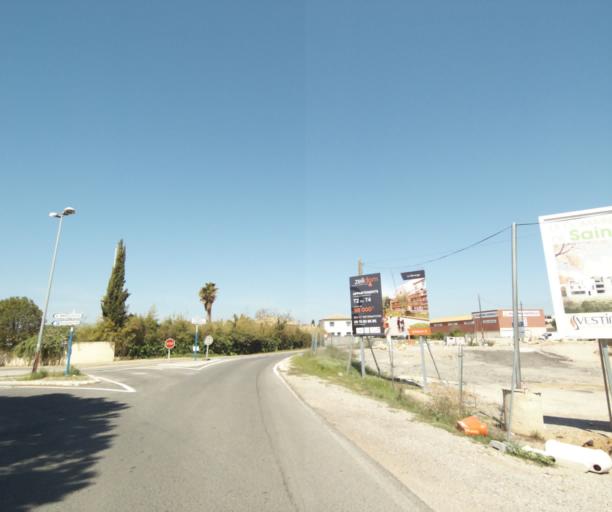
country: FR
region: Languedoc-Roussillon
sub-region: Departement de l'Herault
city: Saint-Bres
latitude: 43.6664
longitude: 4.0385
